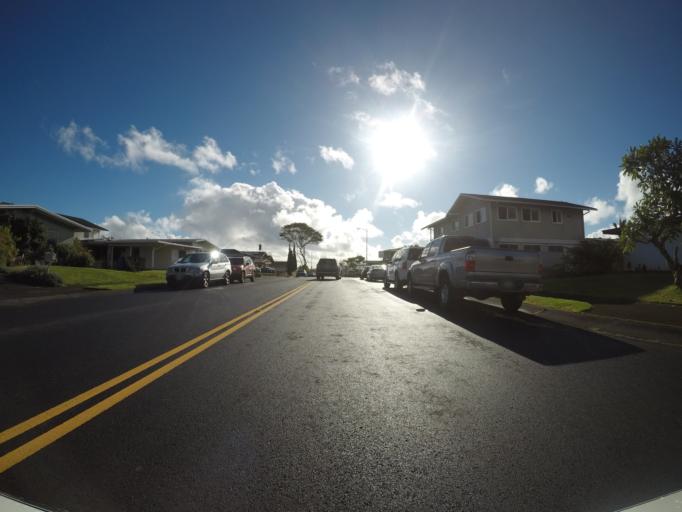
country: US
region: Hawaii
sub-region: Honolulu County
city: He'eia
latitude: 21.4243
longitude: -157.8080
